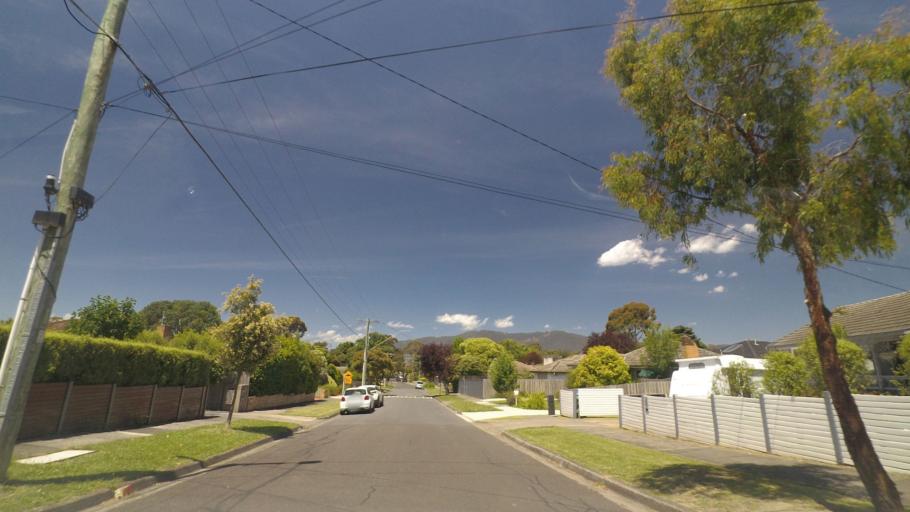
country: AU
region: Victoria
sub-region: Maroondah
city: Bayswater North
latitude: -37.8107
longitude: 145.2894
